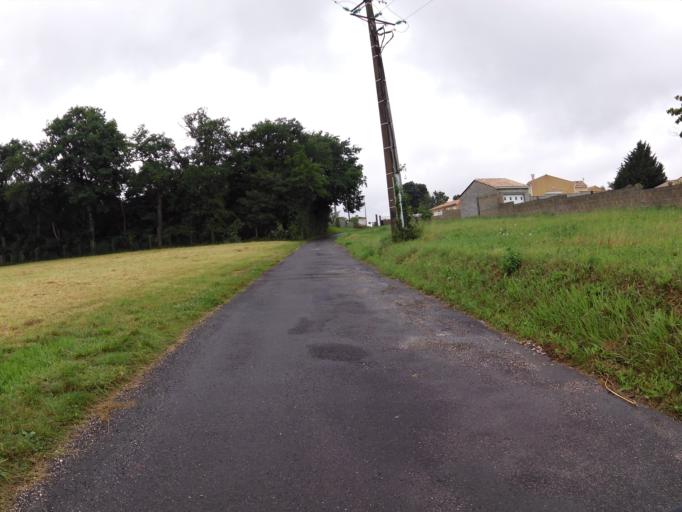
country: FR
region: Poitou-Charentes
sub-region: Departement de la Charente
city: Balzac
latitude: 45.7098
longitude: 0.1405
